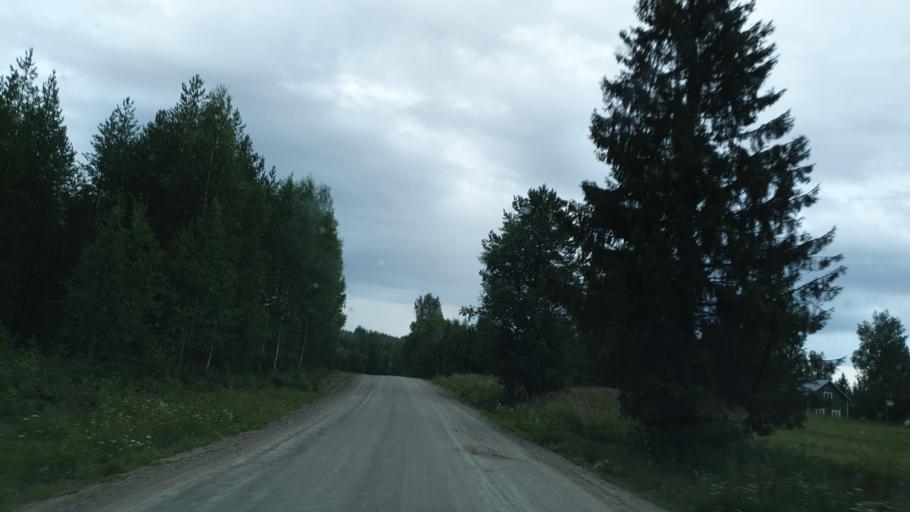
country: FI
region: Kainuu
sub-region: Kehys-Kainuu
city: Kuhmo
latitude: 64.2062
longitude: 29.3716
